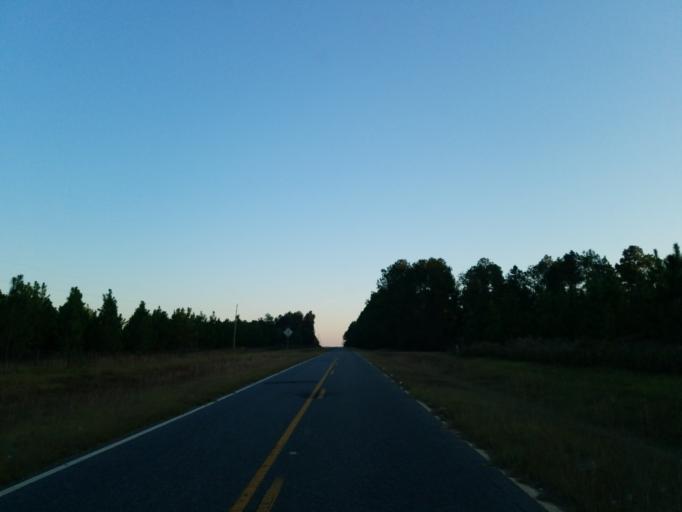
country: US
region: Georgia
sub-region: Ben Hill County
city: Fitzgerald
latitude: 31.7020
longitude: -83.4175
